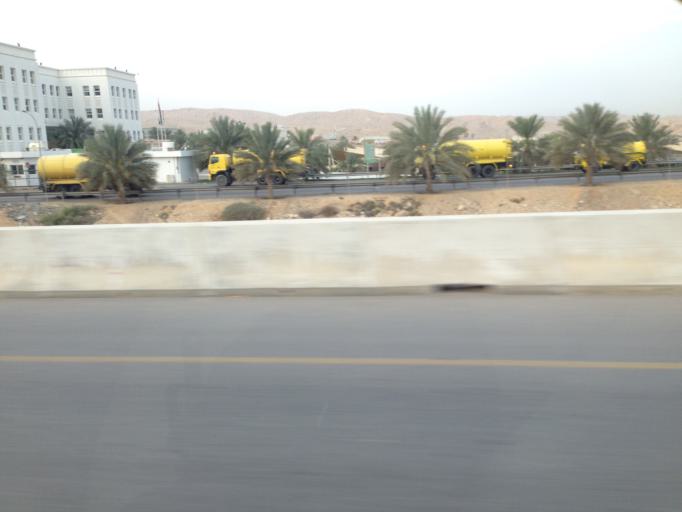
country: OM
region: Muhafazat Masqat
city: Bawshar
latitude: 23.5664
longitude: 58.3374
